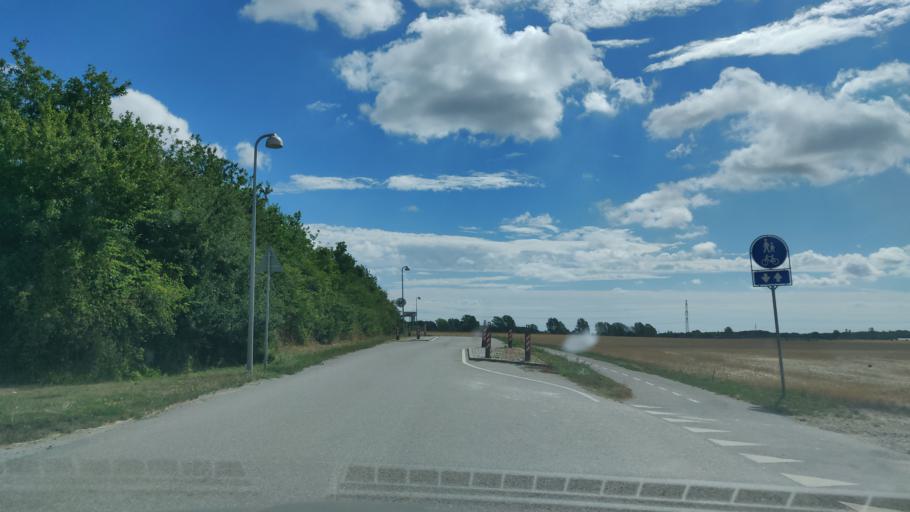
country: DK
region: Capital Region
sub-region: Hoje-Taastrup Kommune
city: Flong
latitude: 55.6630
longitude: 12.1671
